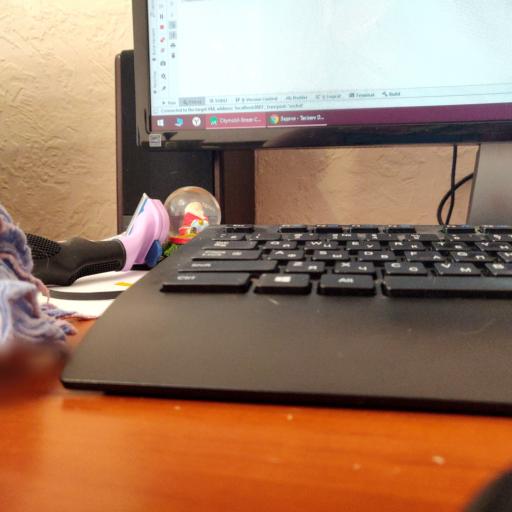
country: FI
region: Haeme
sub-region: Forssa
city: Humppila
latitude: 60.9197
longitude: 23.4344
